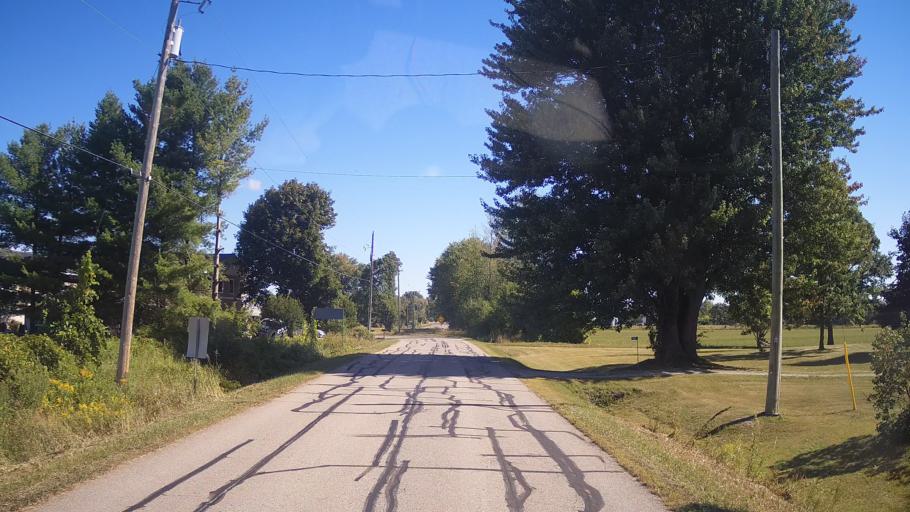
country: CA
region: Ontario
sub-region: Lanark County
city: Smiths Falls
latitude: 44.8400
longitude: -75.8818
